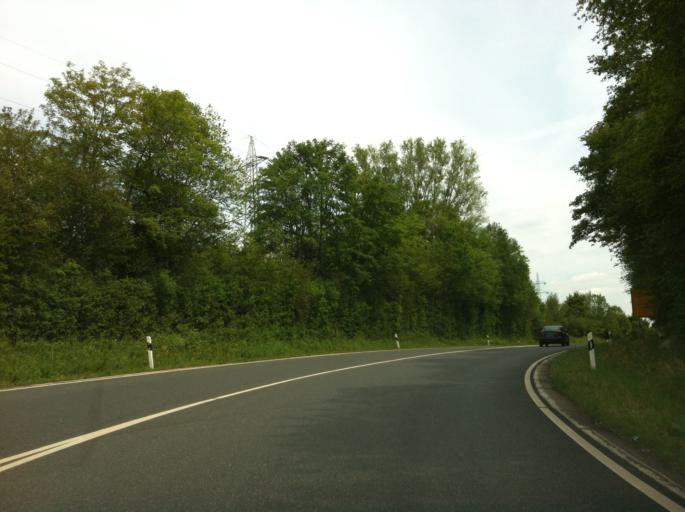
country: DE
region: Hesse
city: Liederbach
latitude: 50.1328
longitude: 8.4898
